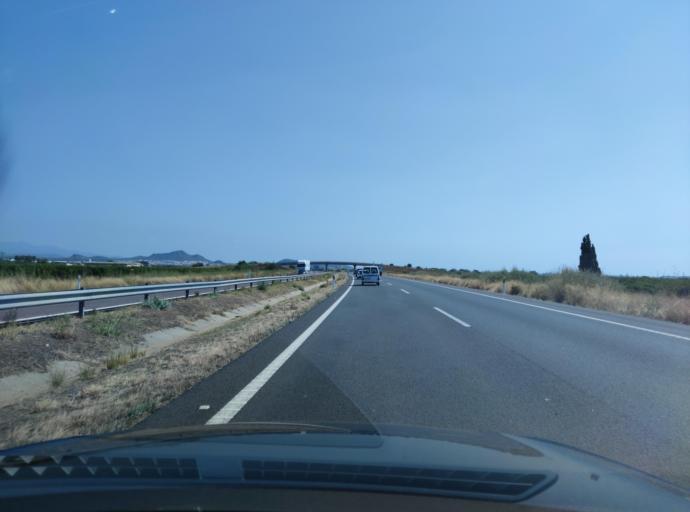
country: ES
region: Valencia
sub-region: Provincia de Valencia
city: Faura
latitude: 39.7079
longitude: -0.2427
